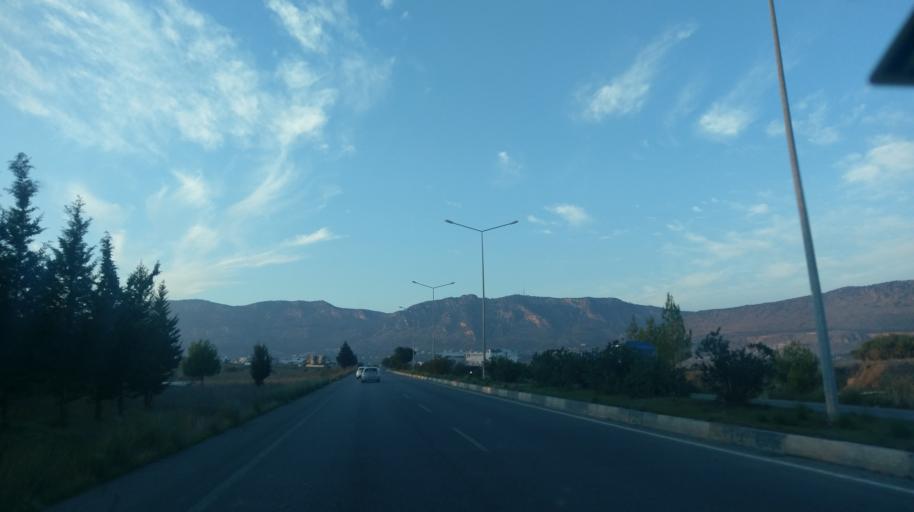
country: CY
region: Keryneia
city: Kyrenia
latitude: 35.2640
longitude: 33.2943
